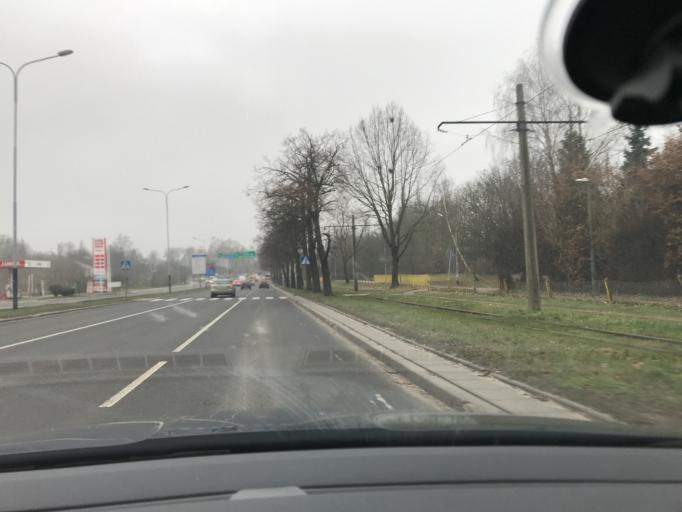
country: PL
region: Lodz Voivodeship
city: Lodz
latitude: 51.7958
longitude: 19.4878
